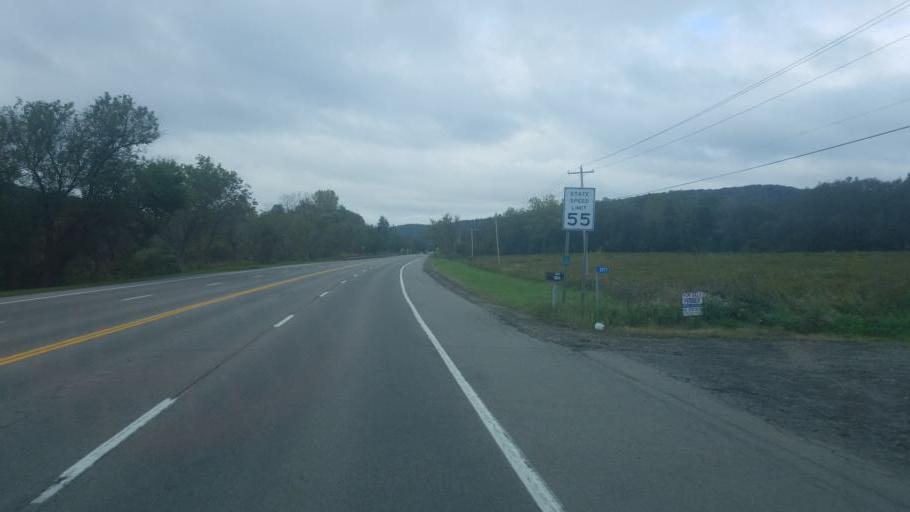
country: US
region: New York
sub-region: Cattaraugus County
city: Weston Mills
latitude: 42.1721
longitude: -78.3851
